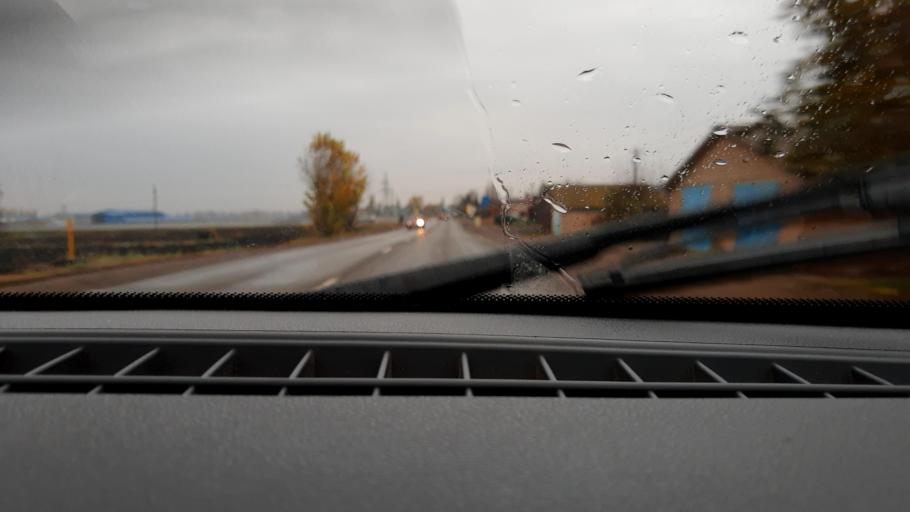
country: RU
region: Bashkortostan
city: Ufa
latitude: 54.8219
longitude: 55.9871
